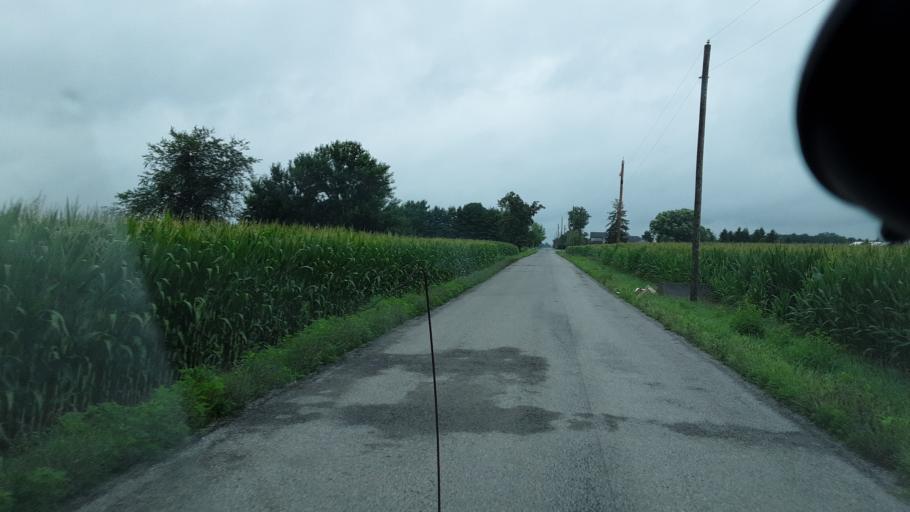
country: US
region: Indiana
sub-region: Wells County
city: Ossian
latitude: 40.9475
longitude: -85.1102
